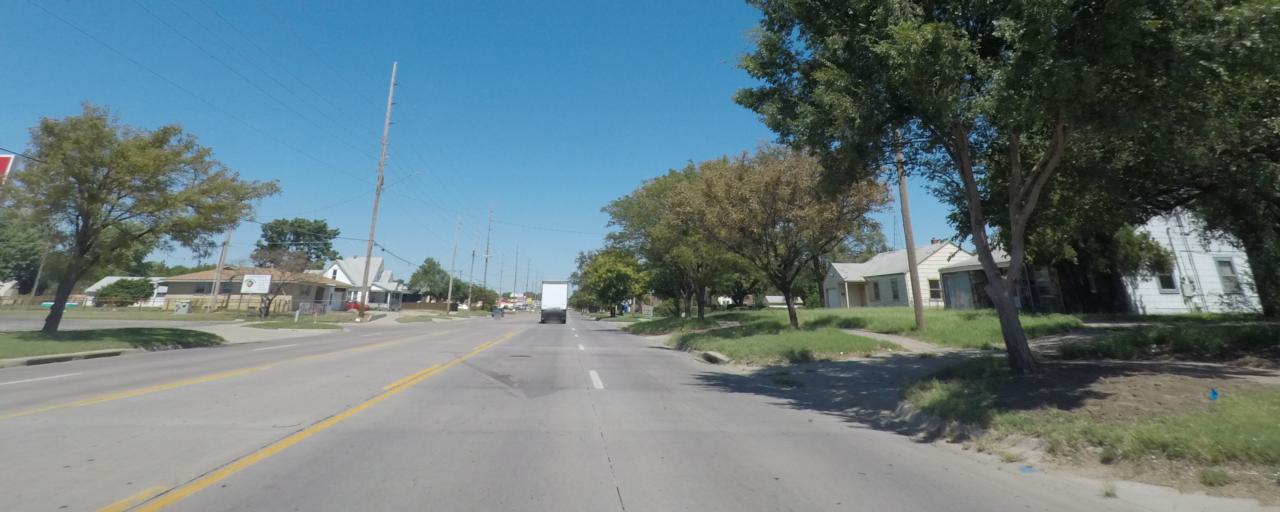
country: US
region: Kansas
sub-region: Sedgwick County
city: Wichita
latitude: 37.6546
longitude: -97.3527
